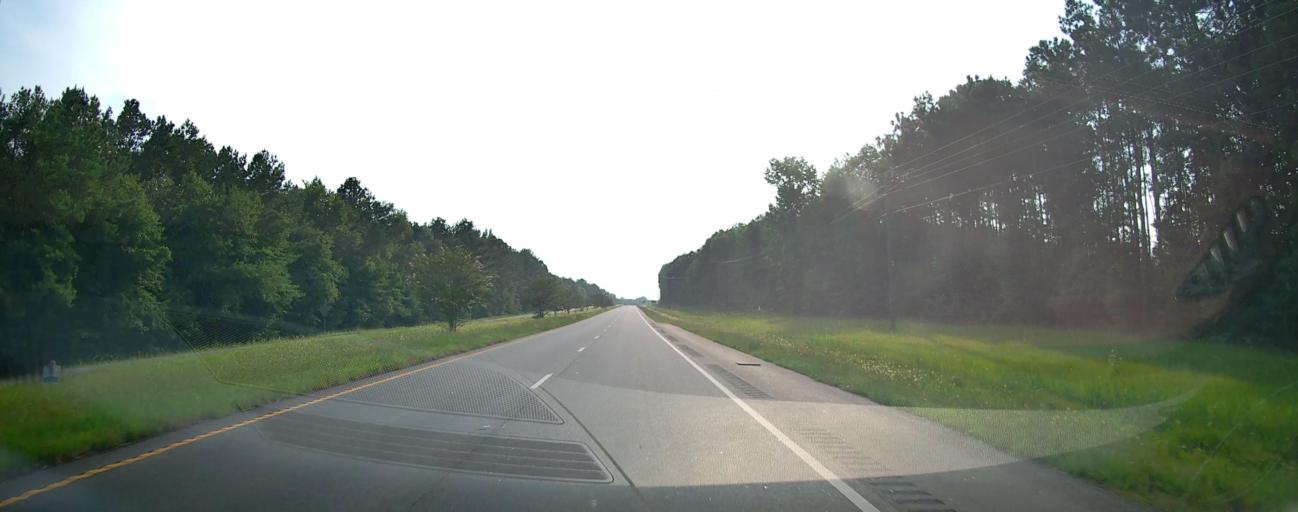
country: US
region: Georgia
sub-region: Talbot County
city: Talbotton
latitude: 32.5459
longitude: -84.7156
